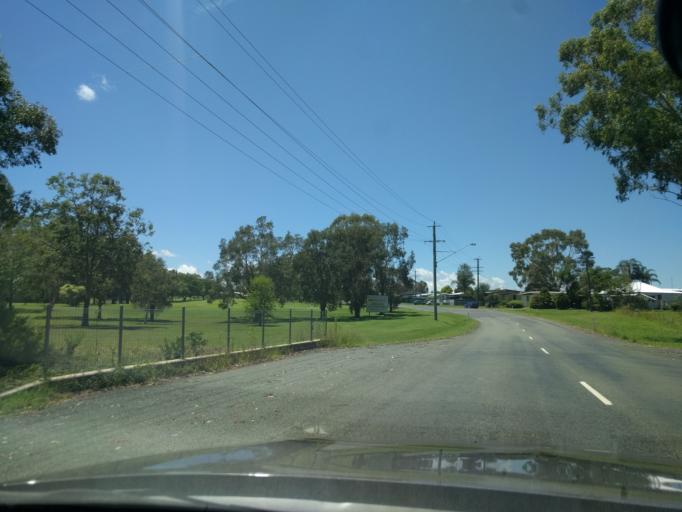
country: AU
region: Queensland
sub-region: Logan
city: Cedar Vale
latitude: -27.9962
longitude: 152.9977
